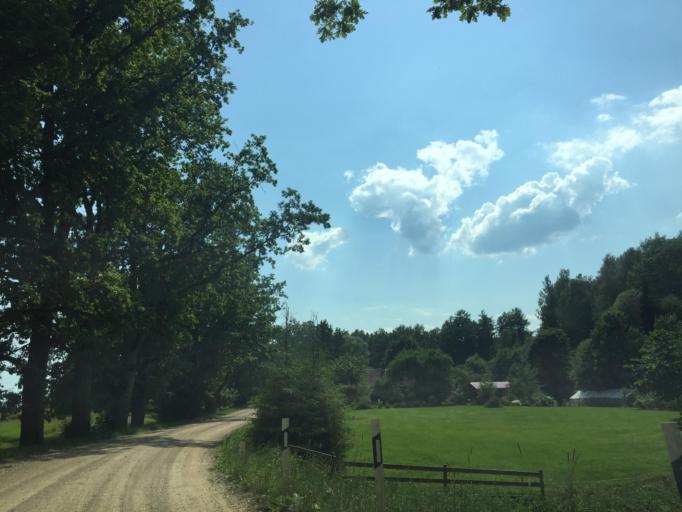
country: LV
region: Pargaujas
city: Stalbe
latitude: 57.3695
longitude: 25.1085
